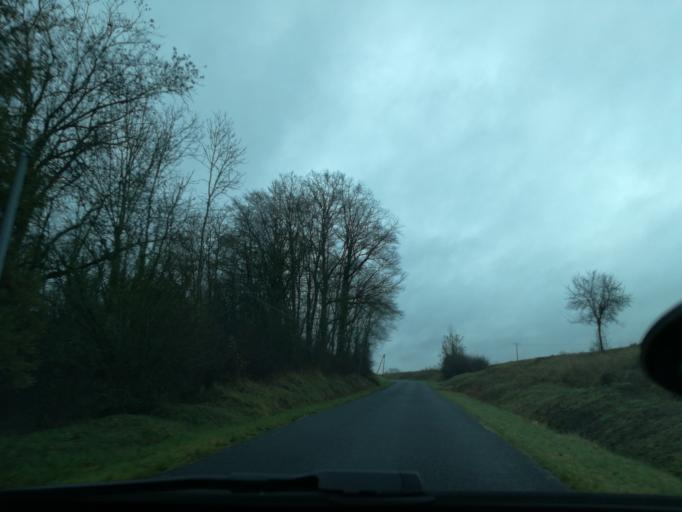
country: FR
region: Lorraine
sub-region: Departement de la Meuse
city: Revigny-sur-Ornain
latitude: 48.8399
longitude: 5.0468
